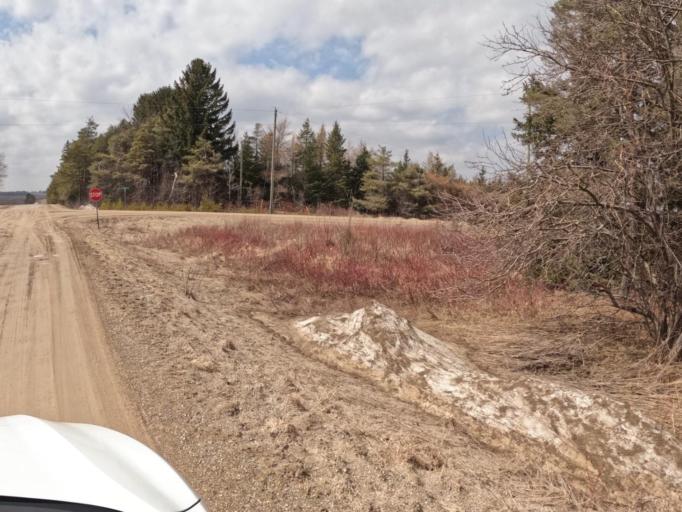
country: CA
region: Ontario
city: Shelburne
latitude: 44.0303
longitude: -80.2420
